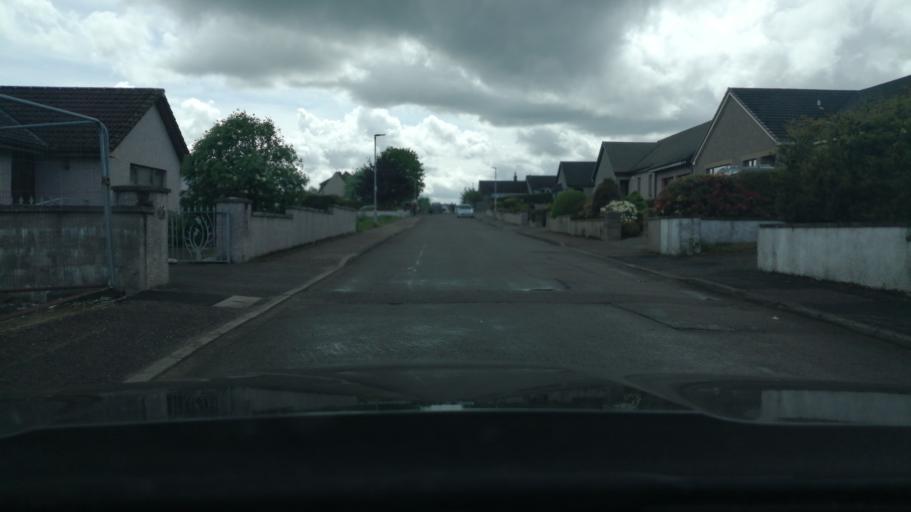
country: GB
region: Scotland
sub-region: Moray
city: Keith
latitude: 57.5412
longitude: -2.9630
